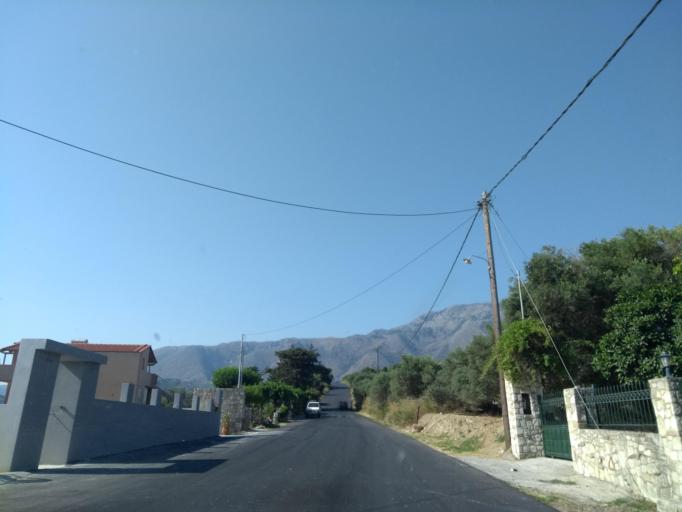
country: GR
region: Crete
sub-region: Nomos Chanias
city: Georgioupolis
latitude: 35.3342
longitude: 24.3016
